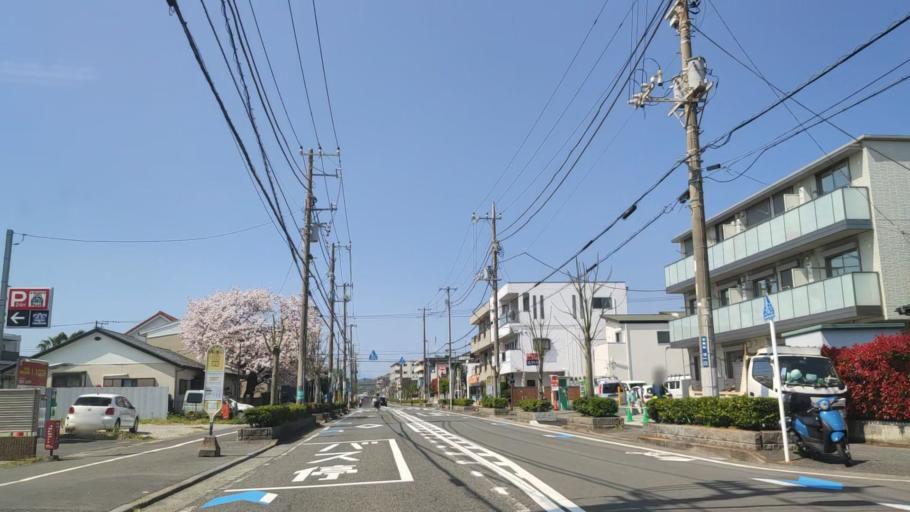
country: JP
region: Kanagawa
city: Hiratsuka
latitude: 35.3204
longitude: 139.3526
